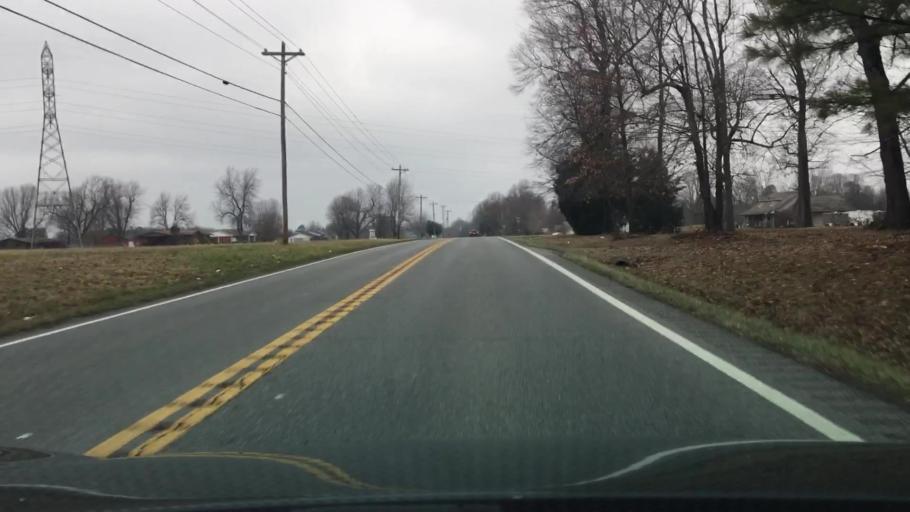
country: US
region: Kentucky
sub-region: Marshall County
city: Calvert City
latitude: 36.9519
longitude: -88.3694
